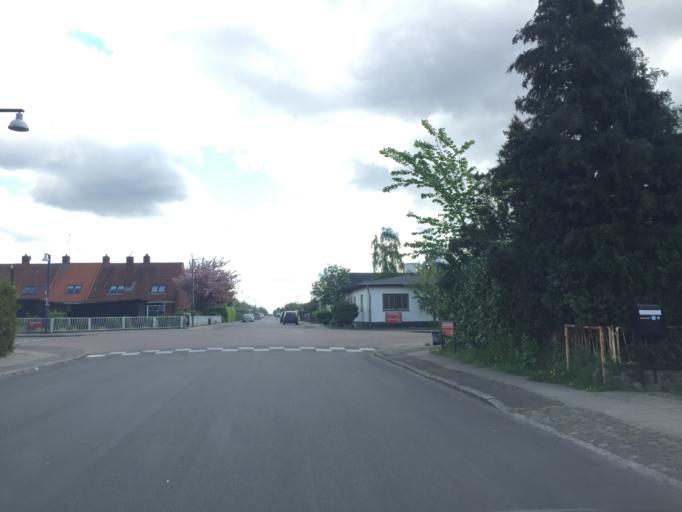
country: DK
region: Capital Region
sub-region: Rodovre Kommune
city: Rodovre
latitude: 55.6857
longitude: 12.4433
